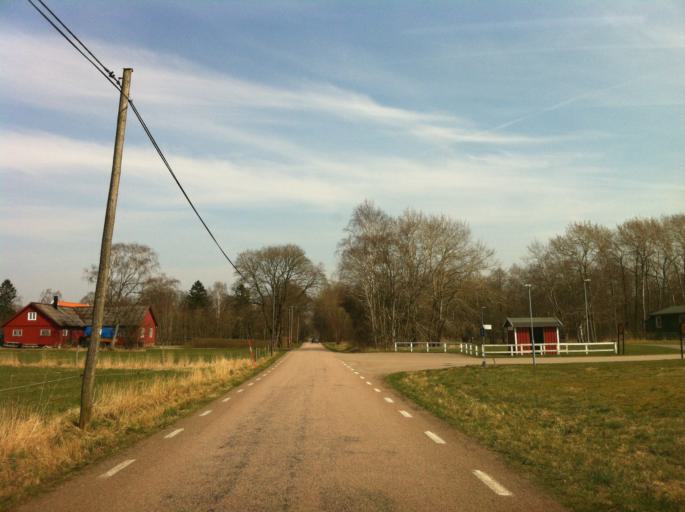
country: SE
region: Skane
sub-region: Klippans Kommun
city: Ljungbyhed
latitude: 55.9959
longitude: 13.2576
